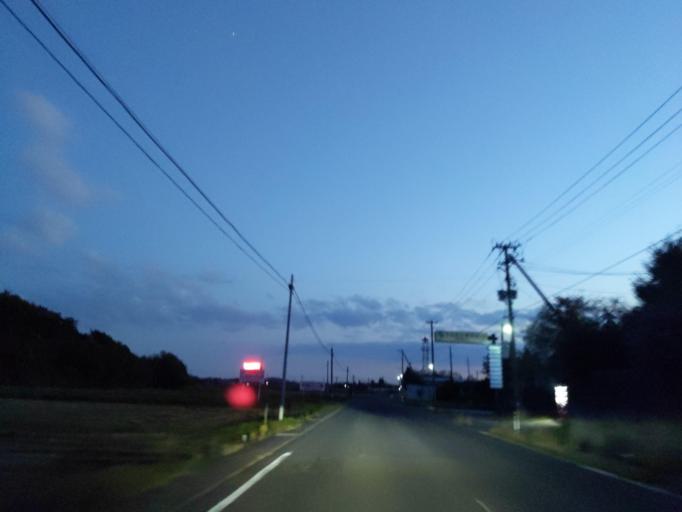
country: JP
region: Fukushima
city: Koriyama
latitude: 37.4383
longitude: 140.3121
